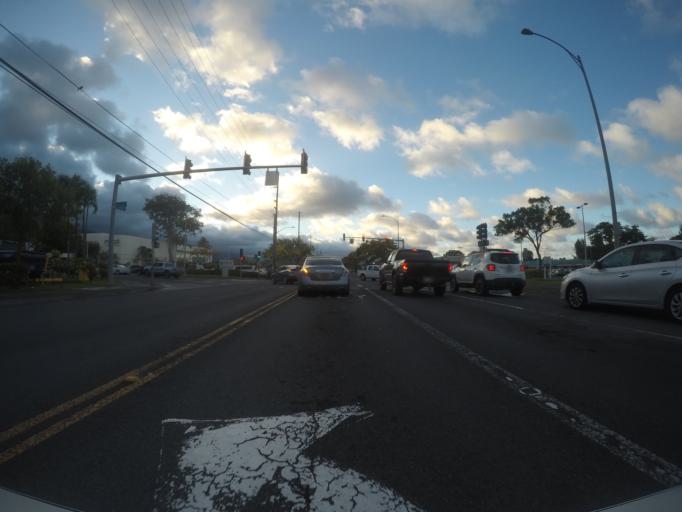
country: US
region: Hawaii
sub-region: Honolulu County
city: He'eia
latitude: 21.4198
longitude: -157.8029
